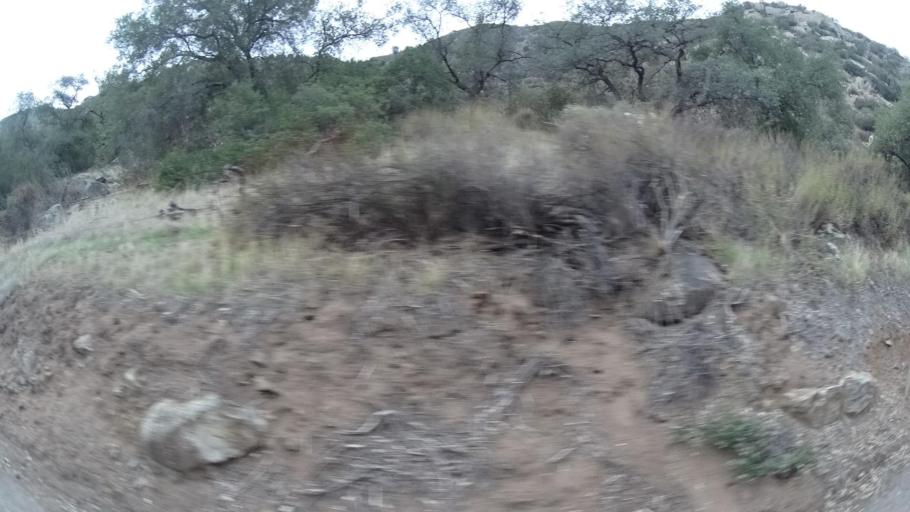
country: US
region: California
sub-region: San Diego County
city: Harbison Canyon
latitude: 32.8878
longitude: -116.8349
